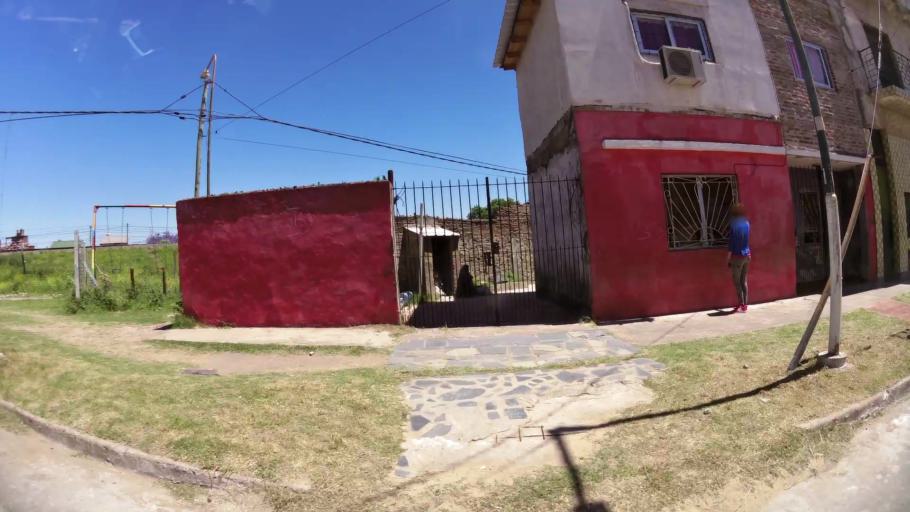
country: AR
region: Buenos Aires
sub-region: Partido de Tigre
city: Tigre
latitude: -34.5061
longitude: -58.5842
